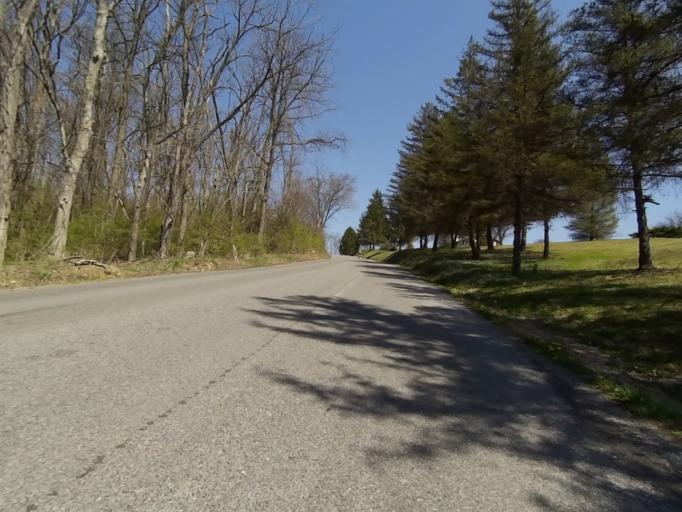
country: US
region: Pennsylvania
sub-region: Blair County
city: Williamsburg
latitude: 40.4778
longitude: -78.1914
